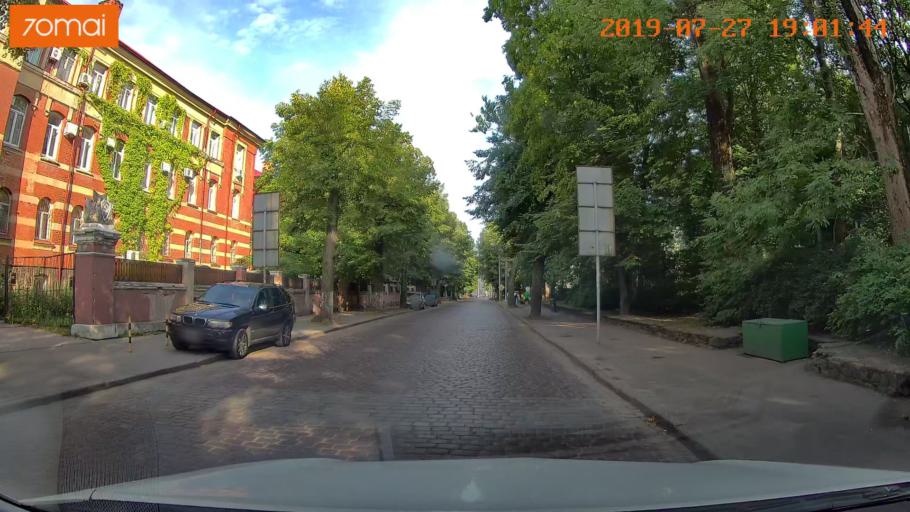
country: RU
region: Kaliningrad
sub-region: Gorod Kaliningrad
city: Kaliningrad
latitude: 54.7259
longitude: 20.4902
